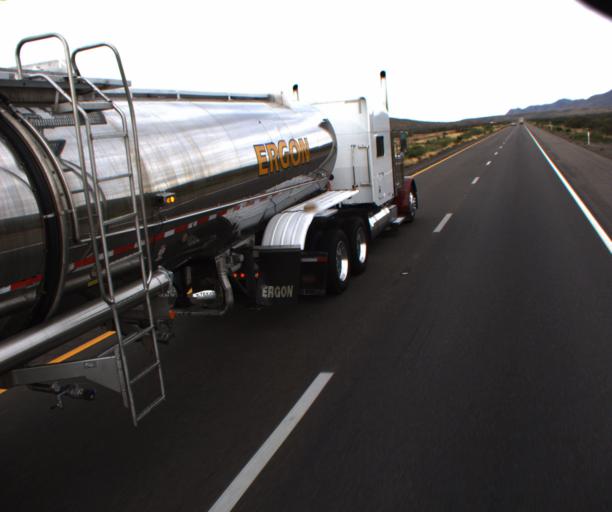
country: US
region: Arizona
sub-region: Cochise County
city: Willcox
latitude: 32.1642
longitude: -109.9705
